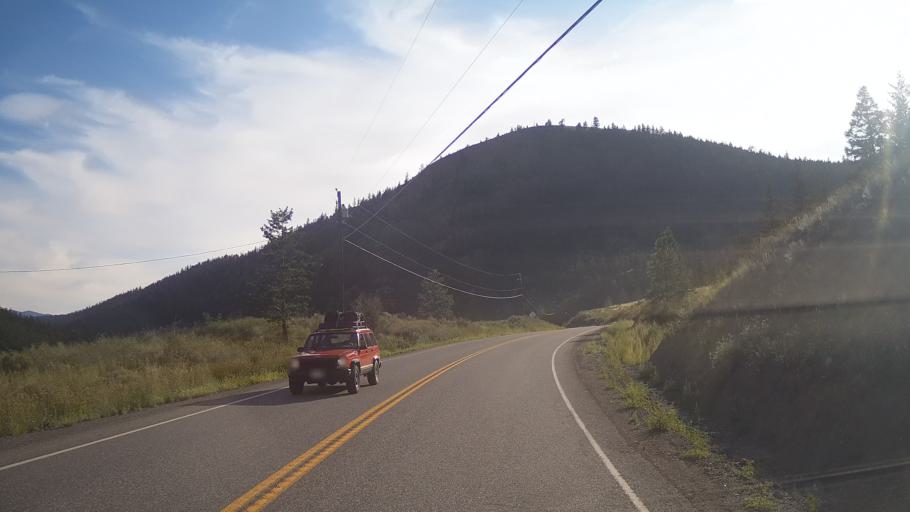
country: CA
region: British Columbia
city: Cache Creek
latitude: 50.8772
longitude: -121.5139
